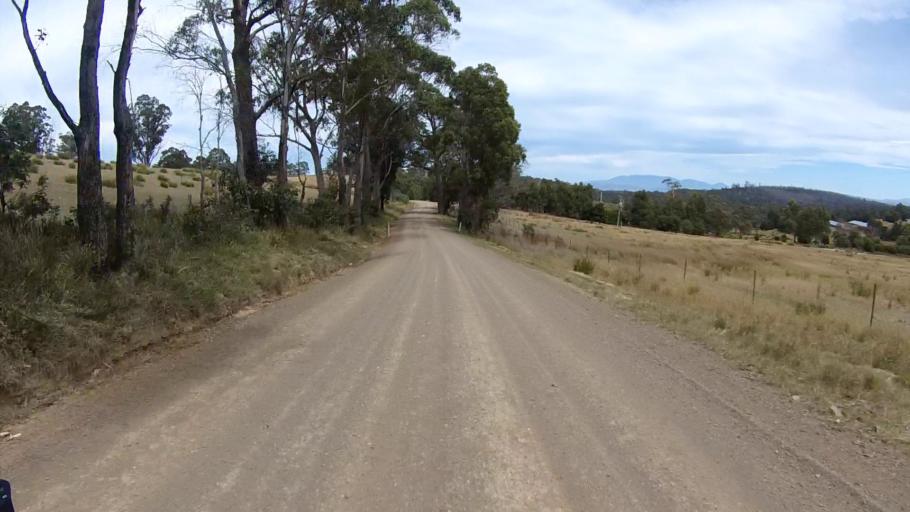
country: AU
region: Tasmania
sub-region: Sorell
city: Sorell
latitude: -42.7902
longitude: 147.6987
